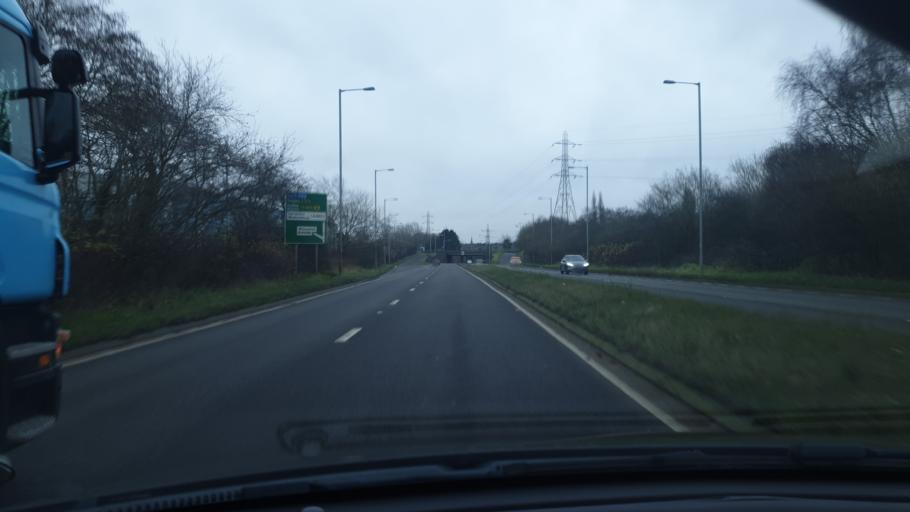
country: GB
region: England
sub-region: Walsall
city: Willenhall
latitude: 52.5792
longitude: -2.0601
